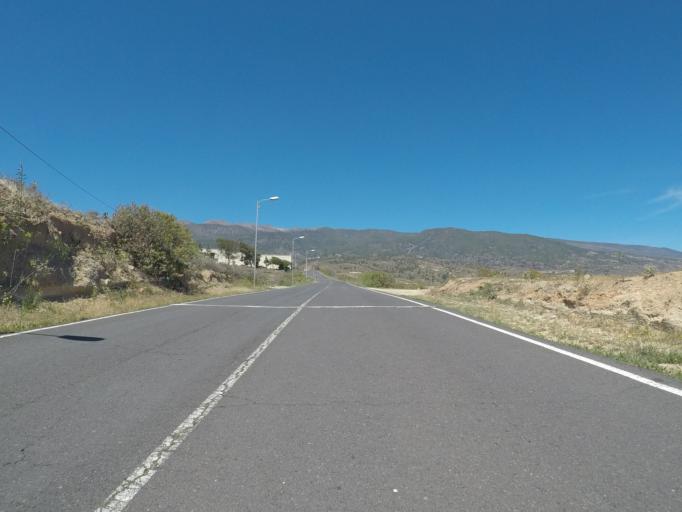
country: ES
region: Canary Islands
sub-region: Provincia de Santa Cruz de Tenerife
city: Lomo de Arico
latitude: 28.1671
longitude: -16.5009
